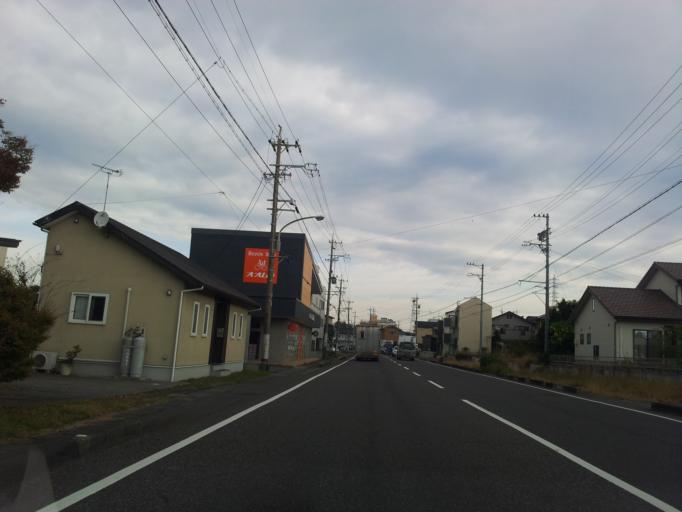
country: JP
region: Shizuoka
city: Shizuoka-shi
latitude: 34.9861
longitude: 138.5086
